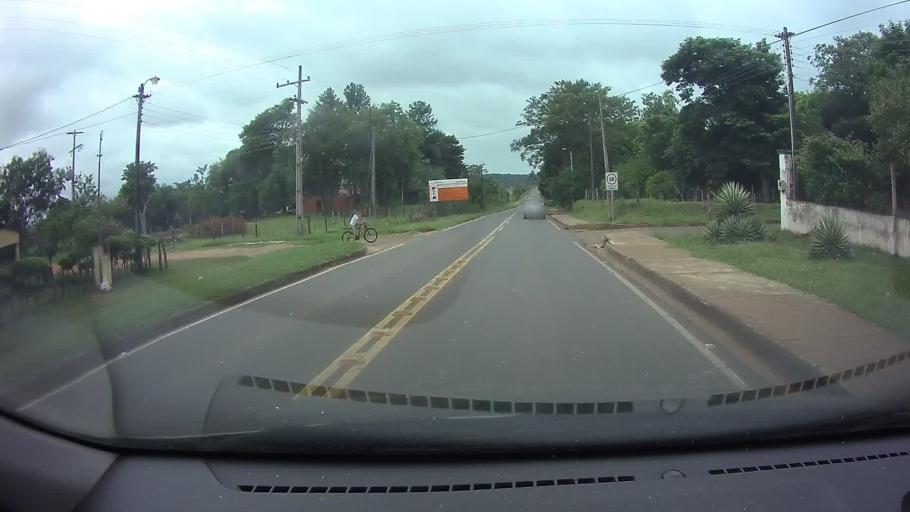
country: PY
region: Central
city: Nueva Italia
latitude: -25.6102
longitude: -57.4605
